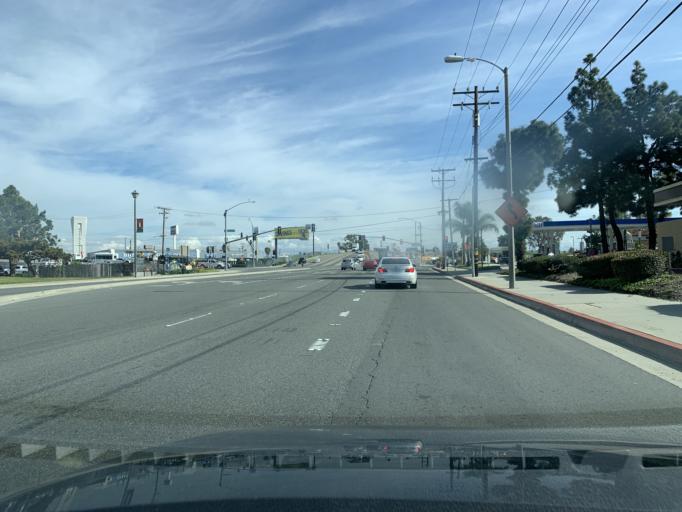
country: US
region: California
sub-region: Orange County
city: Westminster
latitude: 33.7444
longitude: -118.0083
